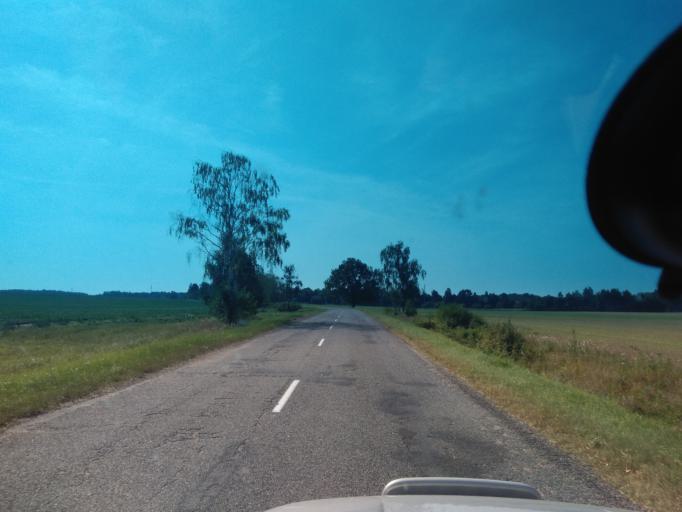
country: BY
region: Minsk
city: Kapyl'
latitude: 53.2347
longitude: 27.1711
